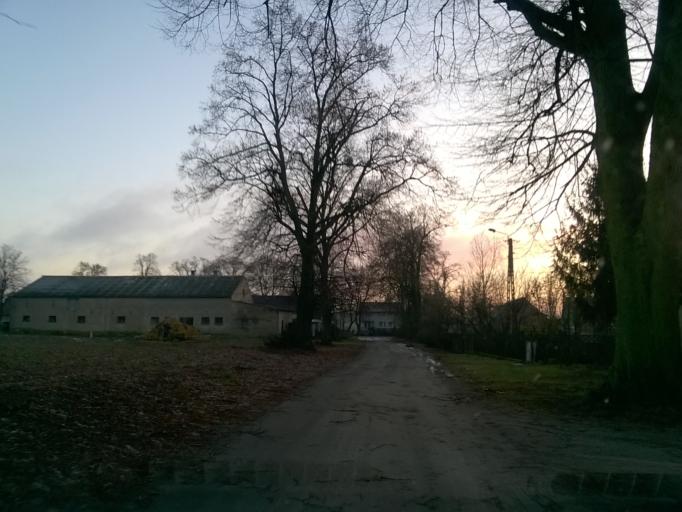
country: PL
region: Kujawsko-Pomorskie
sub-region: Powiat nakielski
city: Kcynia
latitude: 53.0259
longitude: 17.4223
